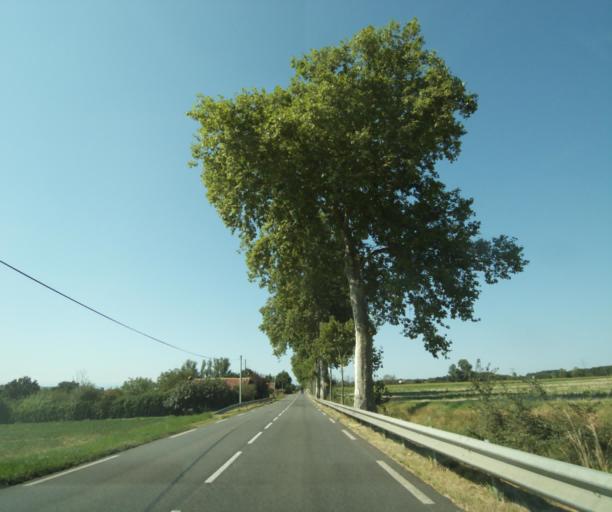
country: FR
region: Midi-Pyrenees
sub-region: Departement de la Haute-Garonne
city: Beaumont-sur-Leze
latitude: 43.3703
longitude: 1.3337
